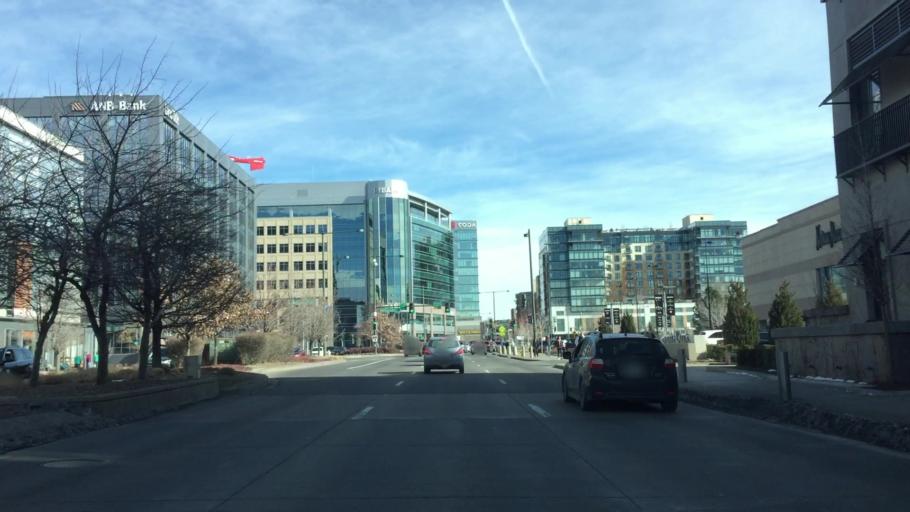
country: US
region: Colorado
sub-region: Arapahoe County
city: Glendale
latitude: 39.7180
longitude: -104.9534
